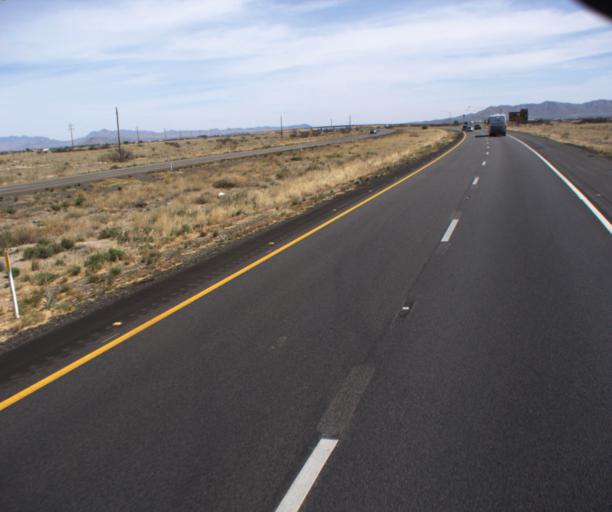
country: US
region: Arizona
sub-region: Cochise County
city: Willcox
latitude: 32.2141
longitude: -109.8859
